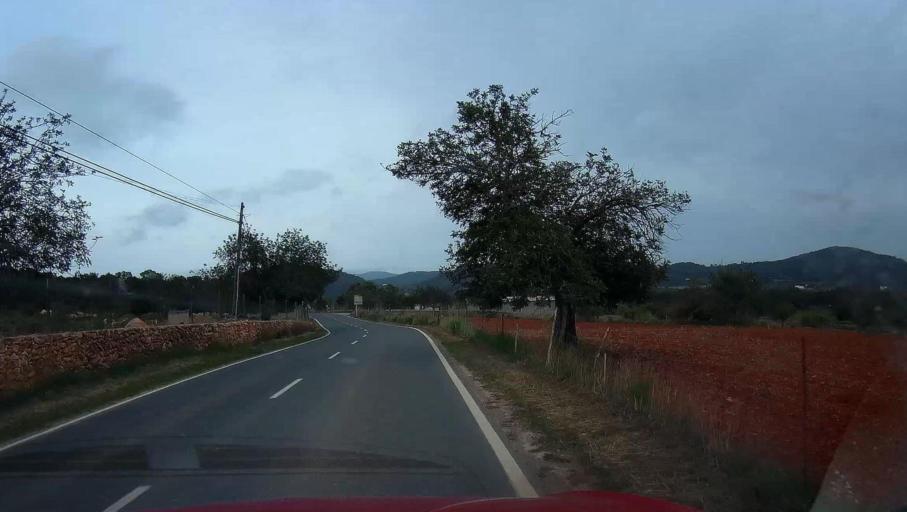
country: ES
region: Balearic Islands
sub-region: Illes Balears
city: Sant Joan de Labritja
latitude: 39.0490
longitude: 1.4267
